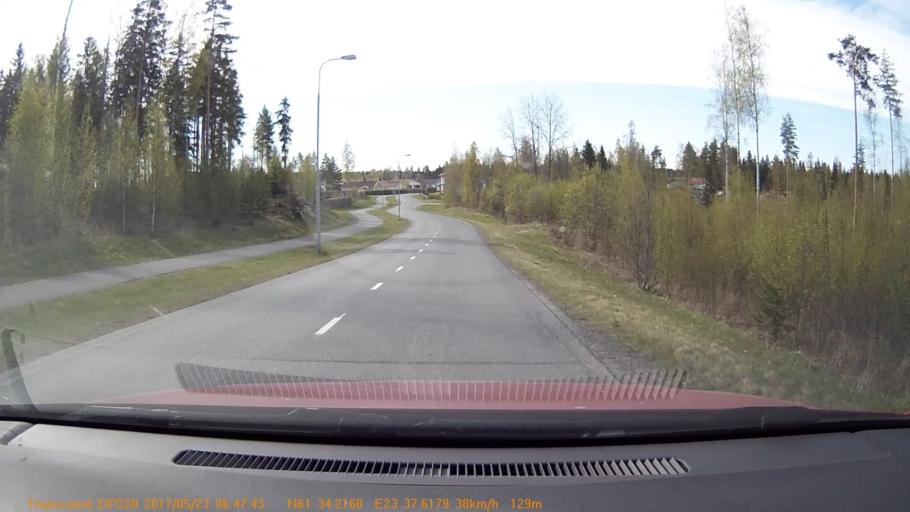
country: FI
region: Pirkanmaa
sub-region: Tampere
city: Yloejaervi
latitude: 61.5704
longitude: 23.6270
